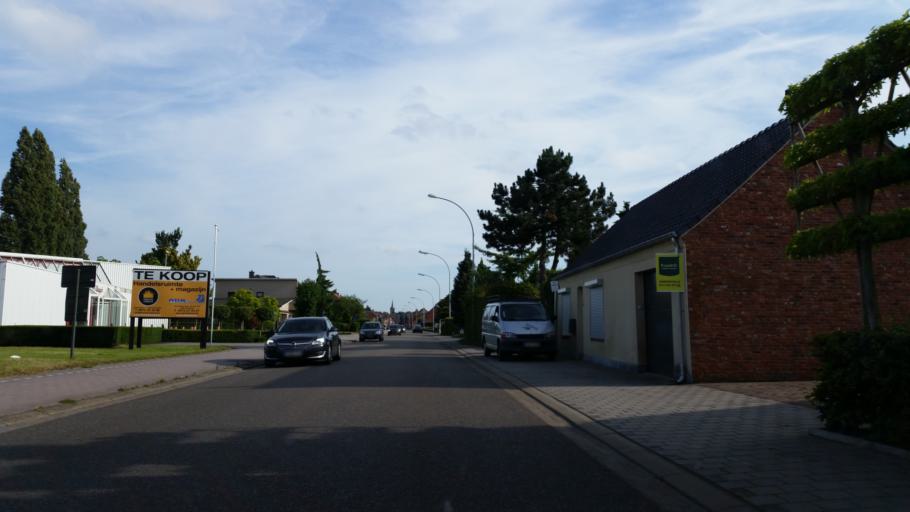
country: BE
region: Flanders
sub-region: Provincie Antwerpen
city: Westerlo
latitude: 51.1134
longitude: 4.9124
